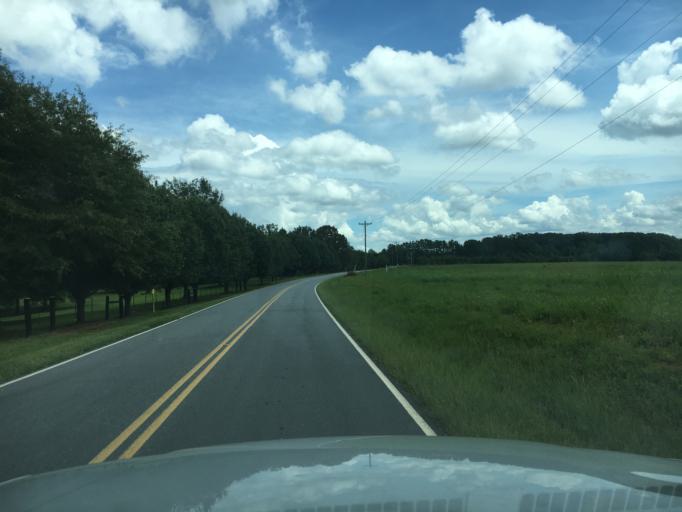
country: US
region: South Carolina
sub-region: Anderson County
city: Belton
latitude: 34.5428
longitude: -82.4510
